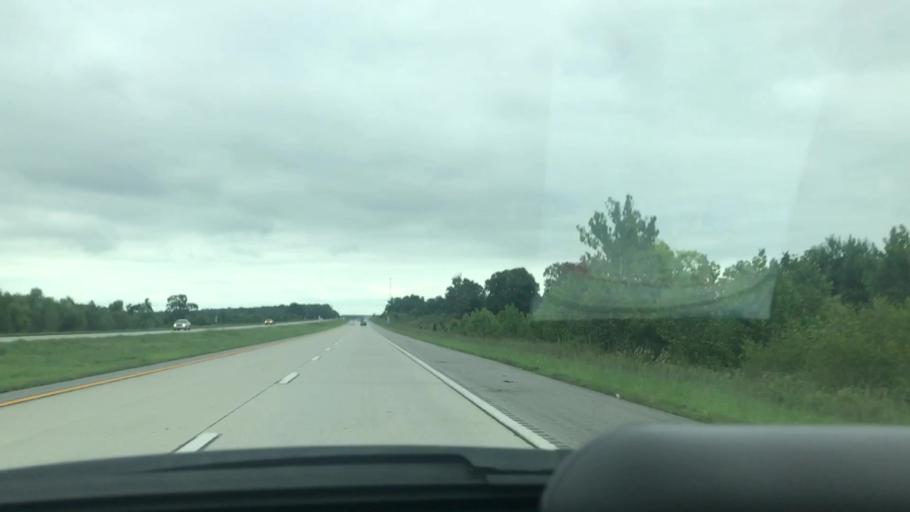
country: US
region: Missouri
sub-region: Greene County
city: Fair Grove
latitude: 37.4927
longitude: -93.1391
